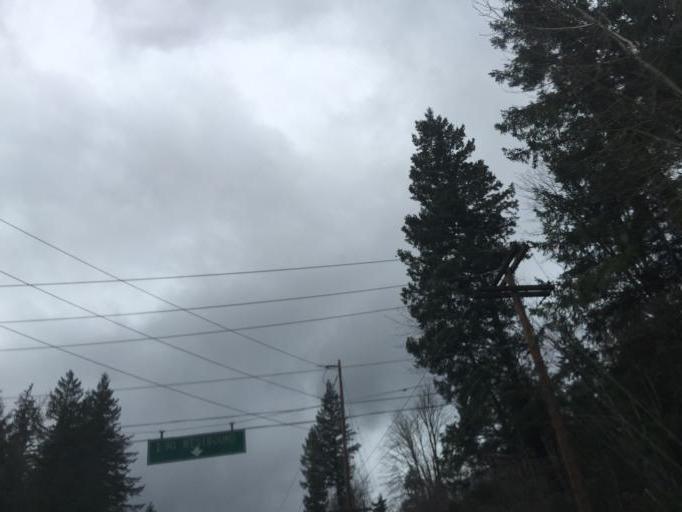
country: US
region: Washington
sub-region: King County
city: Snoqualmie
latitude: 47.5099
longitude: -121.8200
